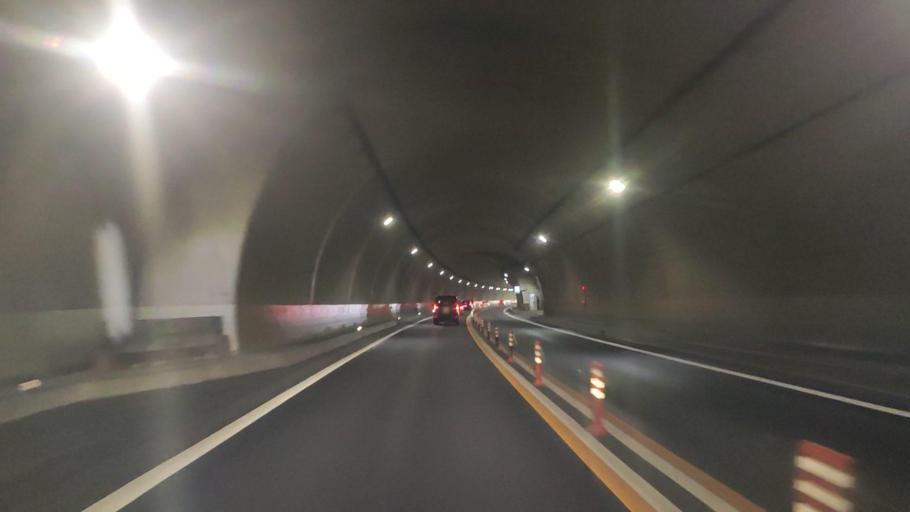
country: JP
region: Fukuoka
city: Nakatsu
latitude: 33.5193
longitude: 131.2599
